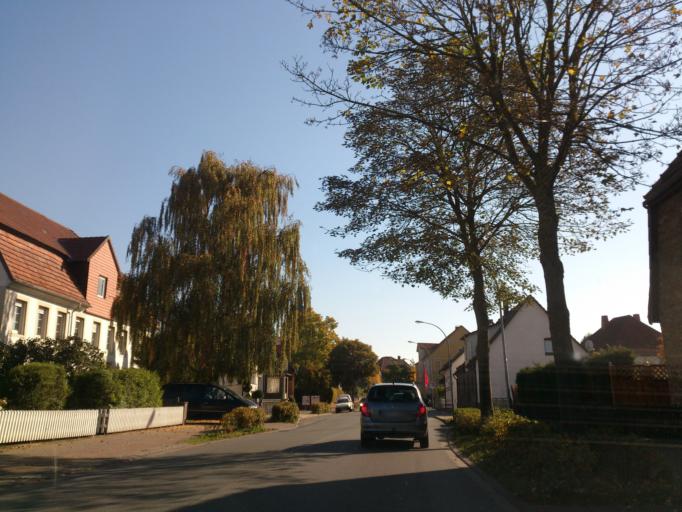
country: DE
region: North Rhine-Westphalia
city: Warburg
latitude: 51.5125
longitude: 9.0836
